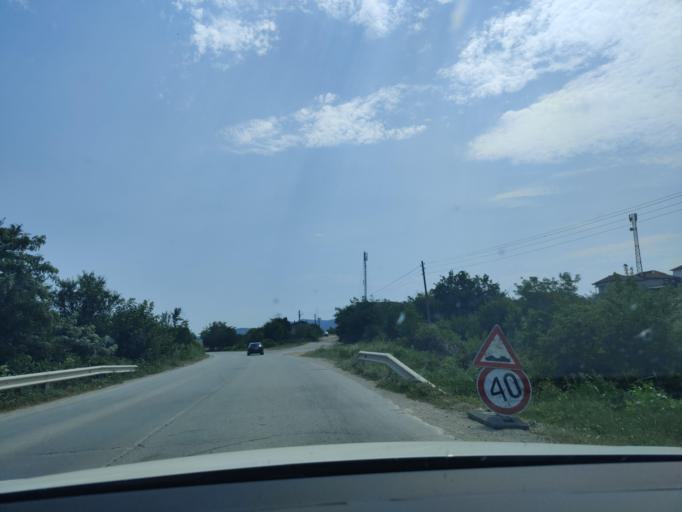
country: BG
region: Montana
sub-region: Obshtina Chiprovtsi
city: Chiprovtsi
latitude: 43.5053
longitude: 22.9854
